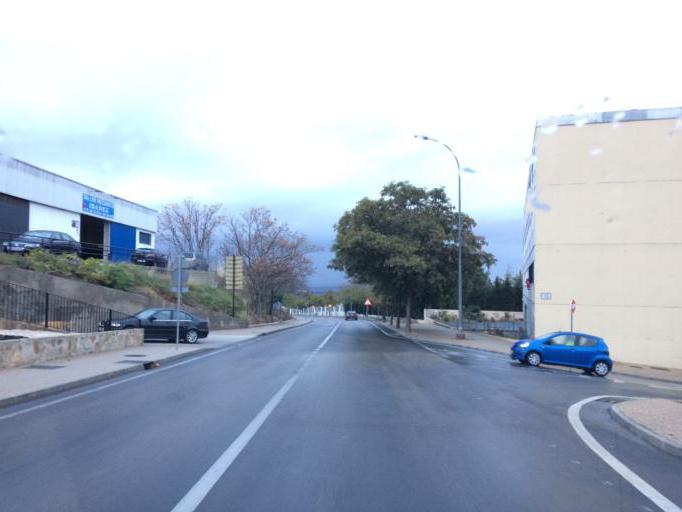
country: ES
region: Andalusia
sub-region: Provincia de Malaga
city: Antequera
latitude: 37.0253
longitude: -4.5617
